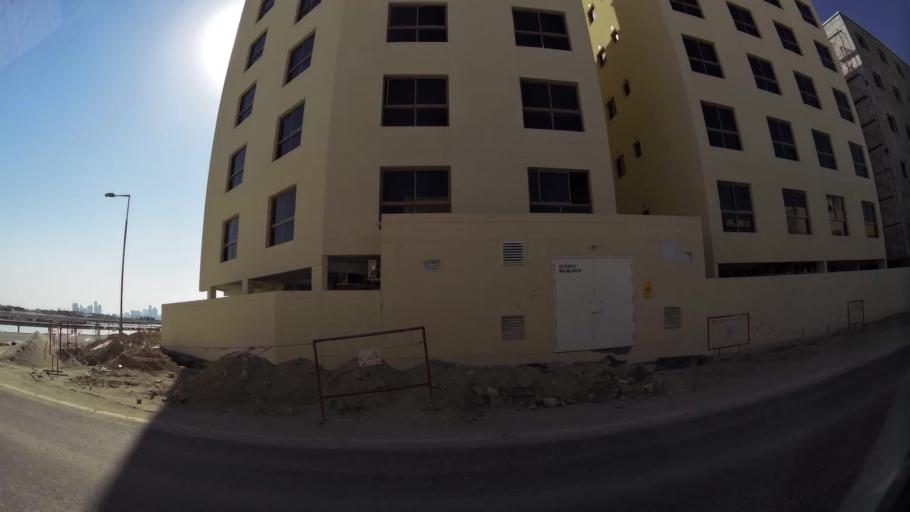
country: BH
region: Muharraq
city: Al Hadd
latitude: 26.2391
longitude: 50.6480
